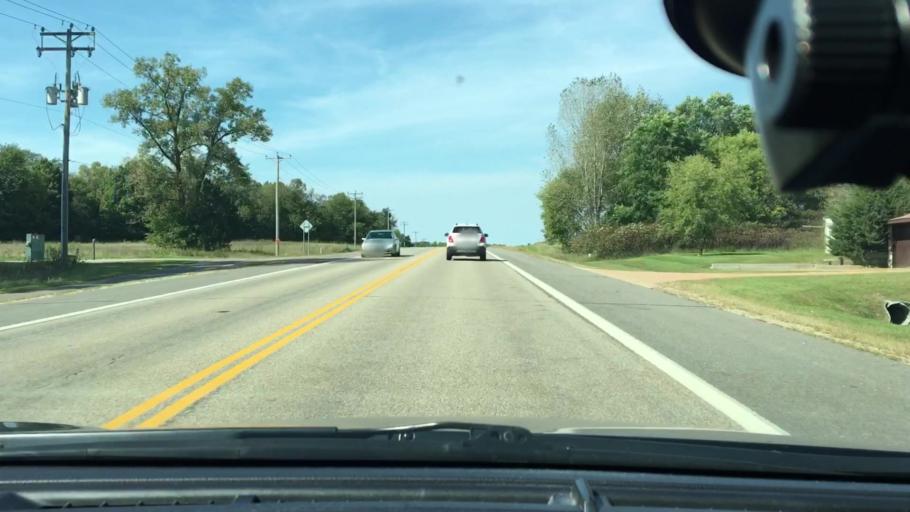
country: US
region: Minnesota
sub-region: Wright County
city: Hanover
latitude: 45.1627
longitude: -93.6693
